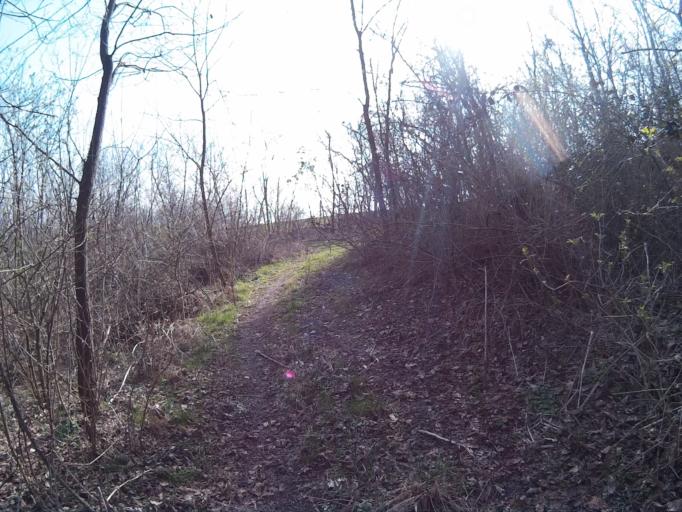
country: HU
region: Nograd
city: Retsag
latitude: 47.8798
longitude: 19.1886
